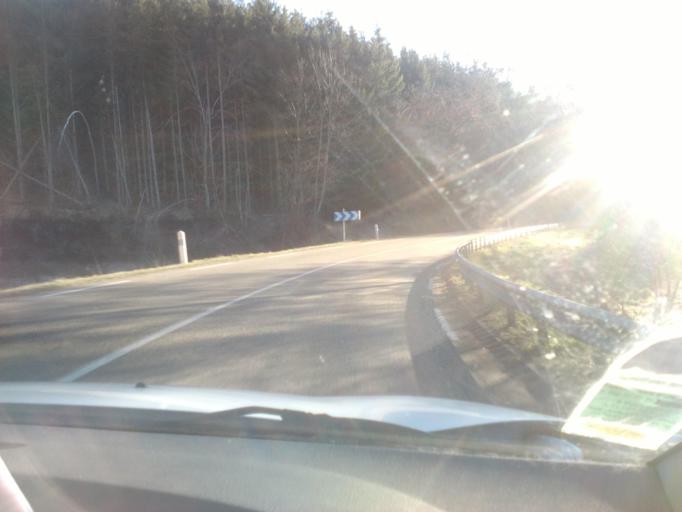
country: FR
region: Alsace
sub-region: Departement du Haut-Rhin
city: Sainte-Marie-aux-Mines
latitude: 48.3523
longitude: 7.1241
